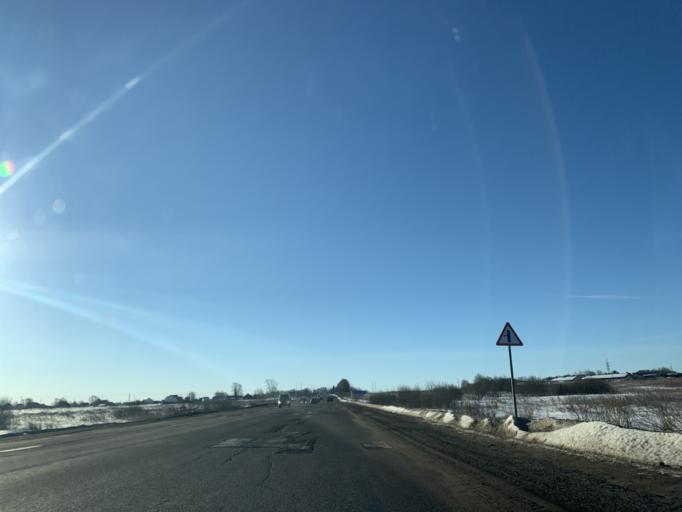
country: RU
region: Jaroslavl
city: Konstantinovskiy
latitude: 57.7945
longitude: 39.6026
